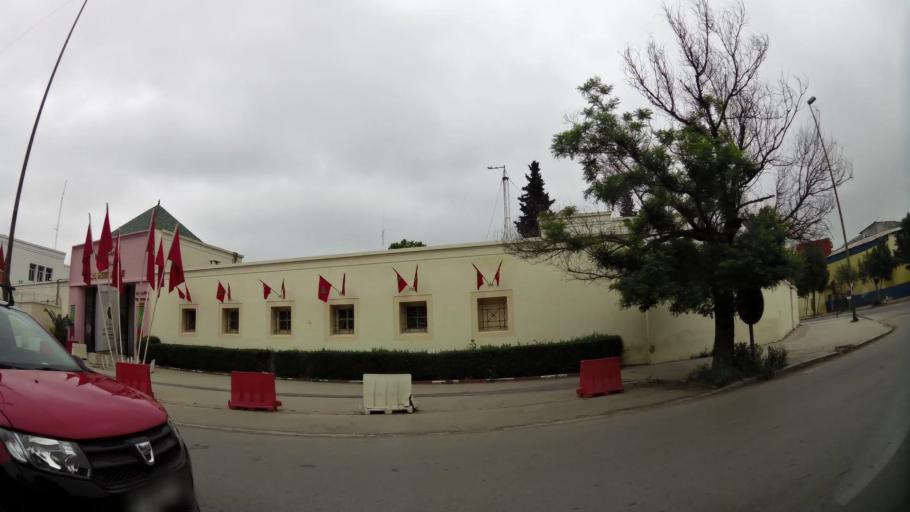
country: MA
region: Fes-Boulemane
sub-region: Fes
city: Fes
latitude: 34.0453
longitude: -5.0010
